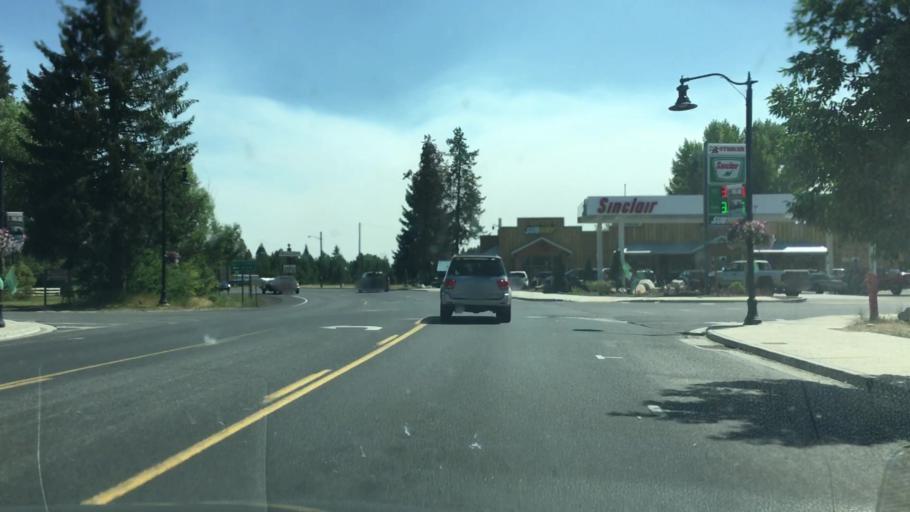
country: US
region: Idaho
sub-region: Valley County
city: McCall
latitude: 44.7312
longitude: -116.0784
